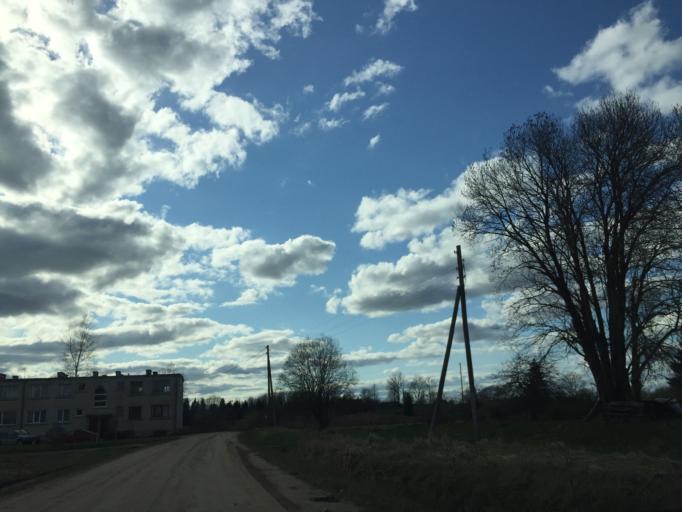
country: LV
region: Rezekne
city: Rezekne
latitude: 56.6097
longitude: 27.3190
